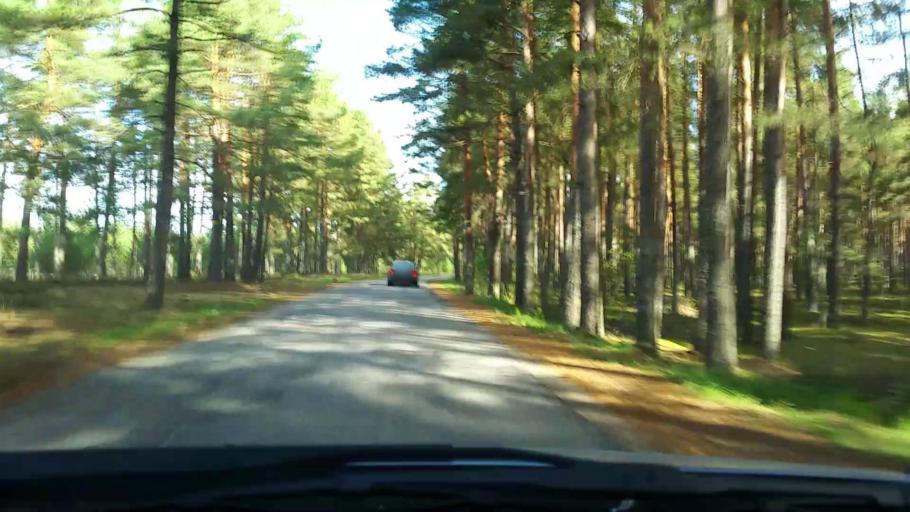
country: LV
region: Adazi
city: Adazi
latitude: 57.1013
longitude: 24.3747
